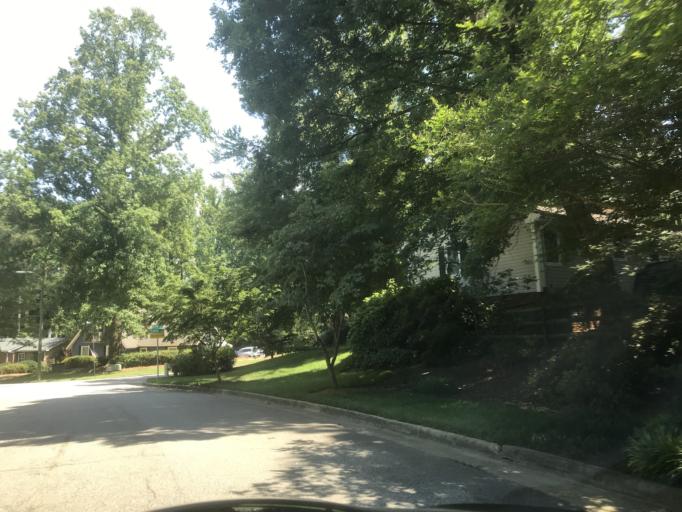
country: US
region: North Carolina
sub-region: Wake County
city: West Raleigh
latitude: 35.8603
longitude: -78.6149
